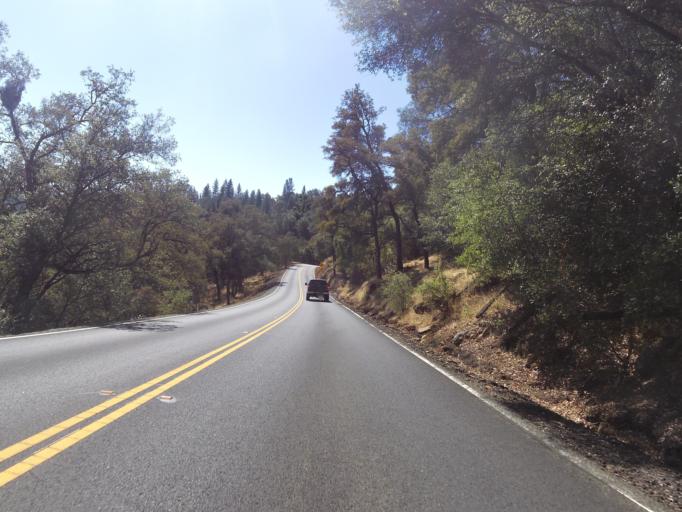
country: US
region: California
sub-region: El Dorado County
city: Deer Park
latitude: 38.6041
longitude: -120.8537
